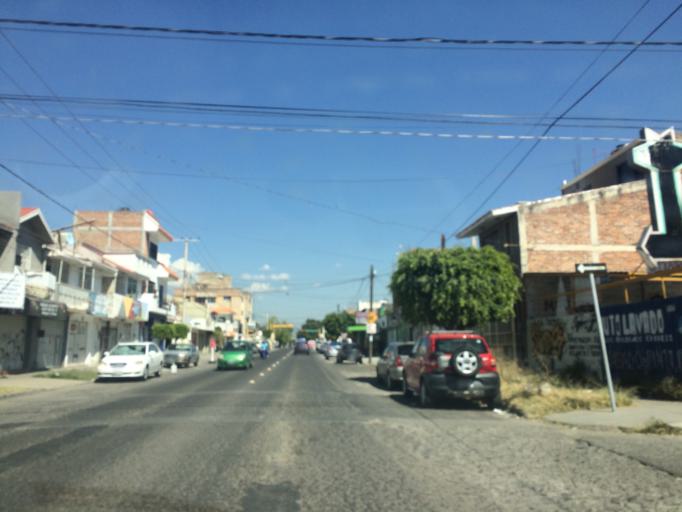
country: MX
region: Guanajuato
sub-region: Leon
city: San Jose de Duran (Los Troncoso)
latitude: 21.0953
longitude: -101.6508
